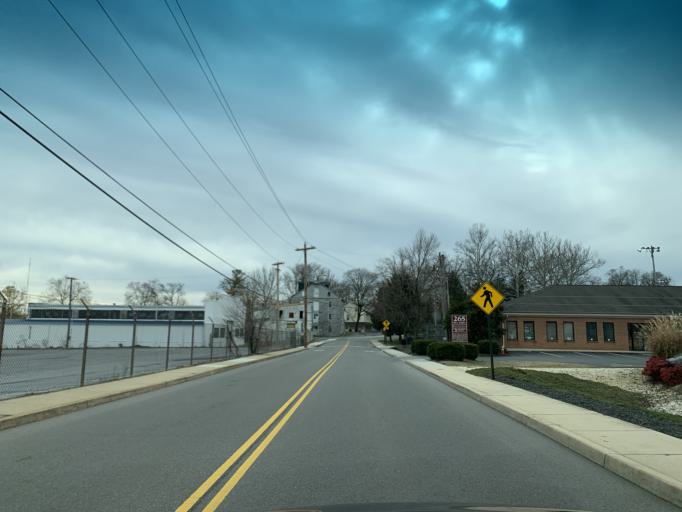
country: US
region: Maryland
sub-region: Washington County
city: Hagerstown
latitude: 39.6346
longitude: -77.7156
